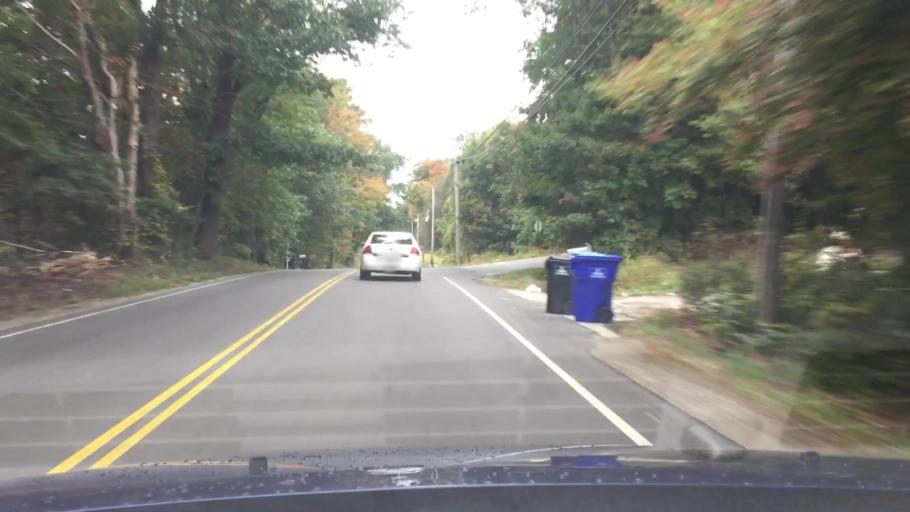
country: US
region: Massachusetts
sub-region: Middlesex County
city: Tyngsboro
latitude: 42.7050
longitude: -71.3958
